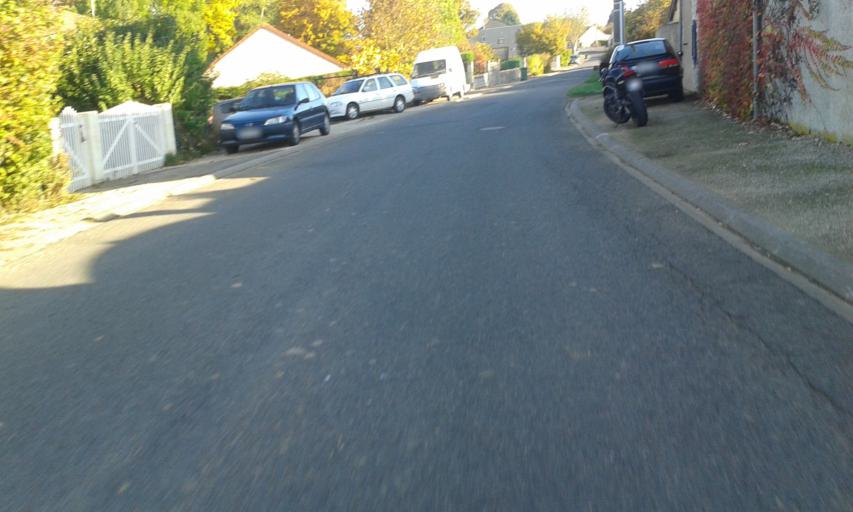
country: FR
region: Centre
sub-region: Departement du Loir-et-Cher
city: Ouzouer-le-Marche
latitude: 47.8828
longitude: 1.4098
